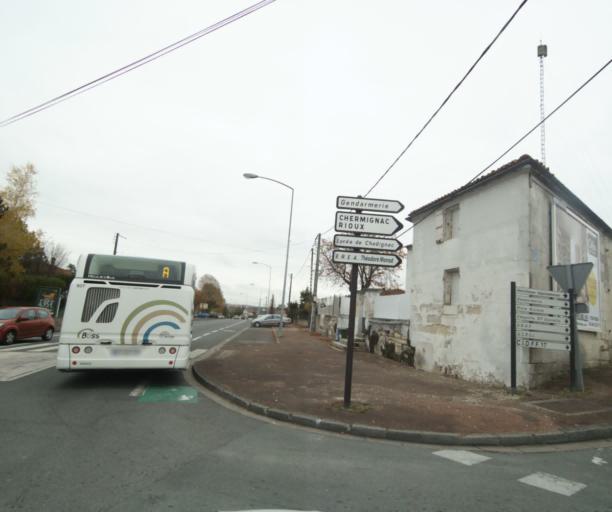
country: FR
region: Poitou-Charentes
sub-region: Departement de la Charente-Maritime
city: Saintes
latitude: 45.7337
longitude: -0.6455
